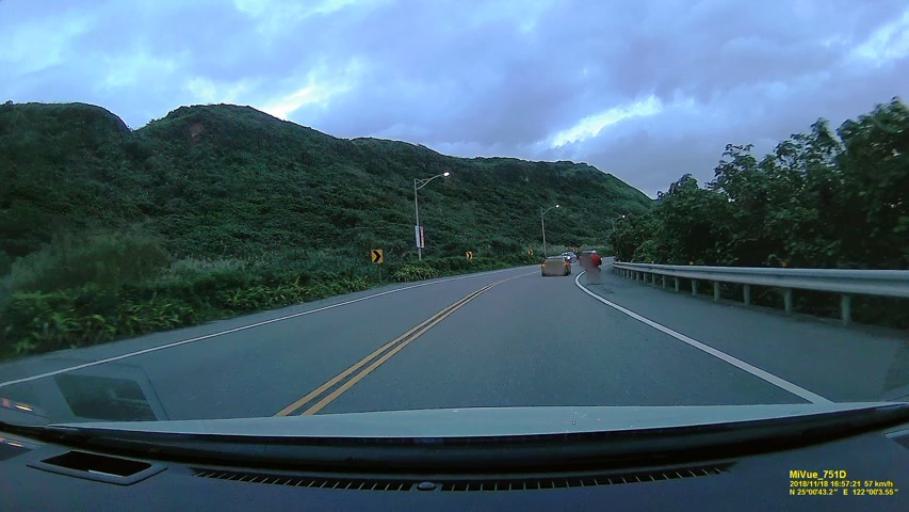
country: TW
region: Taiwan
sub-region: Keelung
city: Keelung
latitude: 25.0122
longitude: 122.0009
